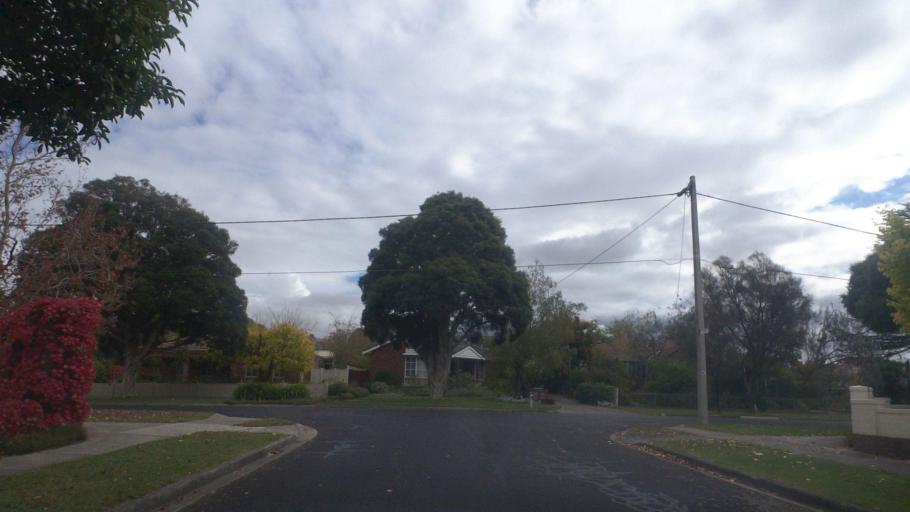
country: AU
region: Victoria
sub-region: Whitehorse
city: Surrey Hills
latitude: -37.8204
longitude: 145.1122
